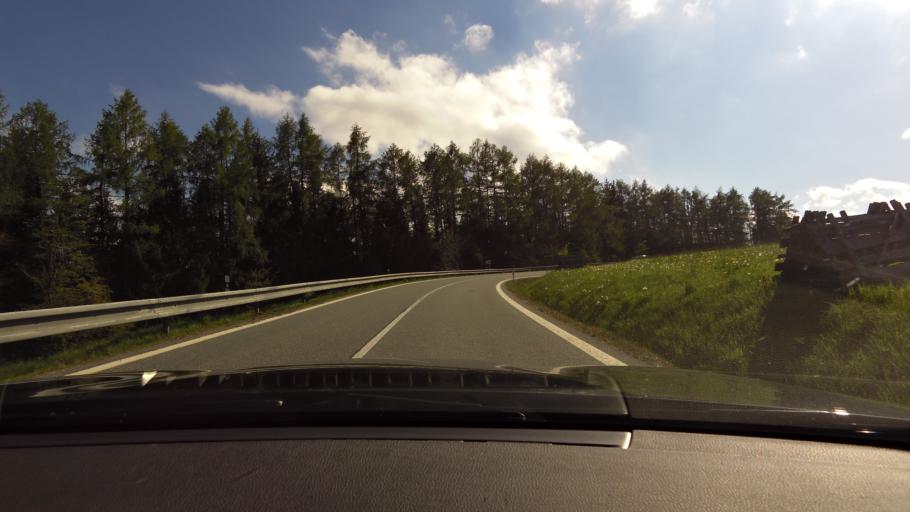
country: CZ
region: Plzensky
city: Strazov
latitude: 49.2486
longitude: 13.3066
